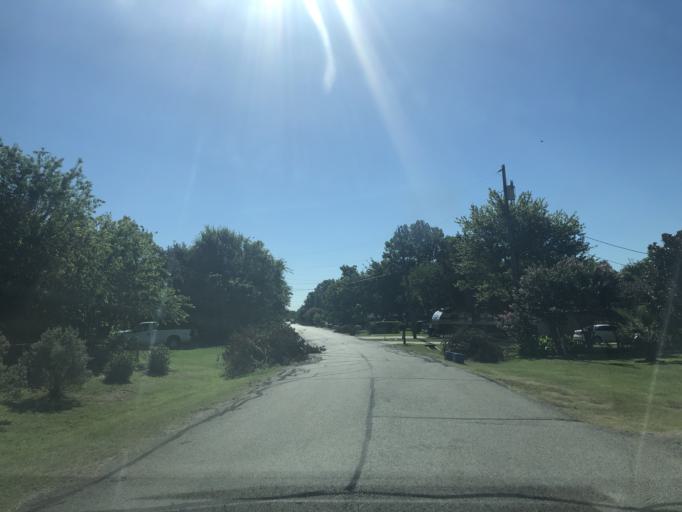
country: US
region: Texas
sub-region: Dallas County
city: Duncanville
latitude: 32.6529
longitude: -96.9404
